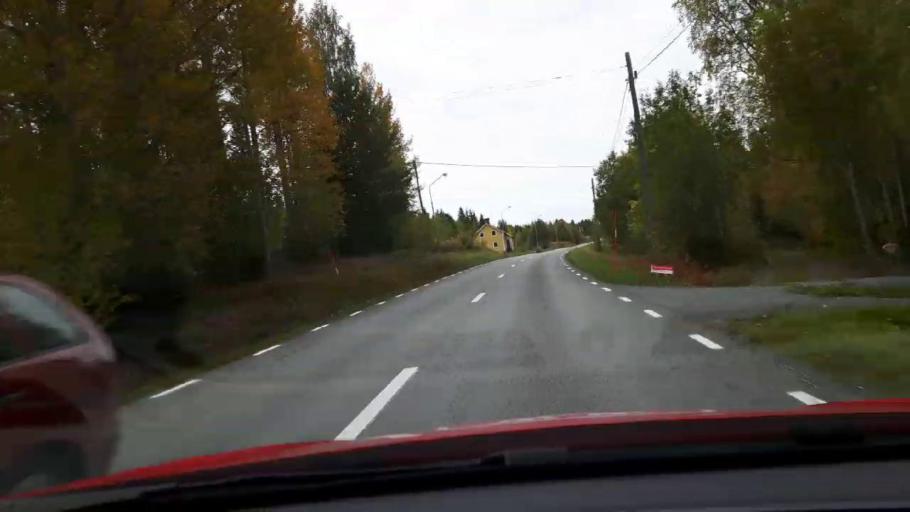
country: SE
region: Jaemtland
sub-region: Krokoms Kommun
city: Krokom
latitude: 63.1848
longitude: 14.0736
